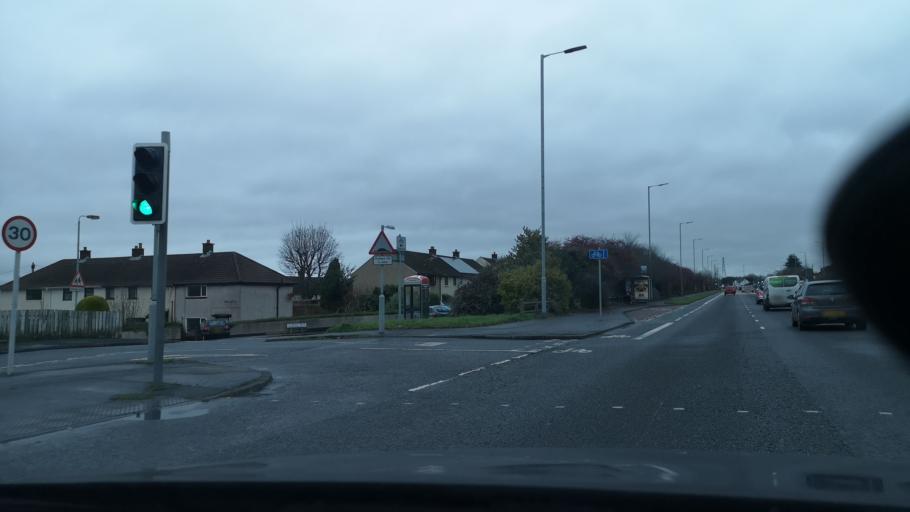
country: GB
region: Northern Ireland
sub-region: Castlereagh District
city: Castlereagh
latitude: 54.5750
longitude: -5.8803
